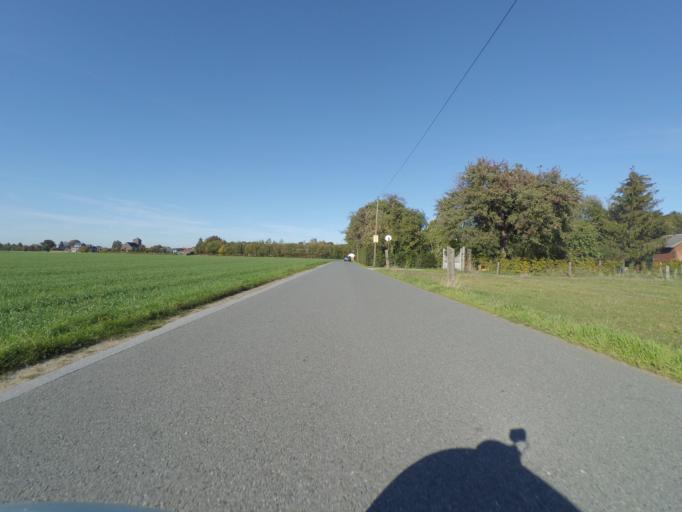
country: DE
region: North Rhine-Westphalia
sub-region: Regierungsbezirk Dusseldorf
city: Bocholt
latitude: 51.8594
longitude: 6.5661
